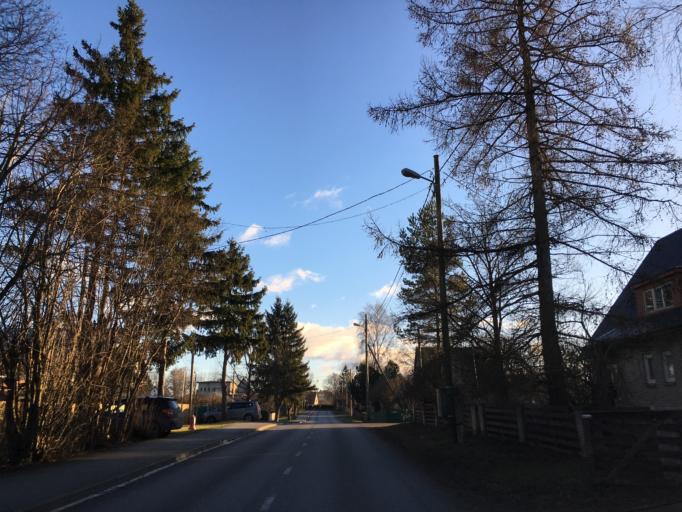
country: EE
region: Harju
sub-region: Saue linn
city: Saue
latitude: 59.3222
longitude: 24.5516
